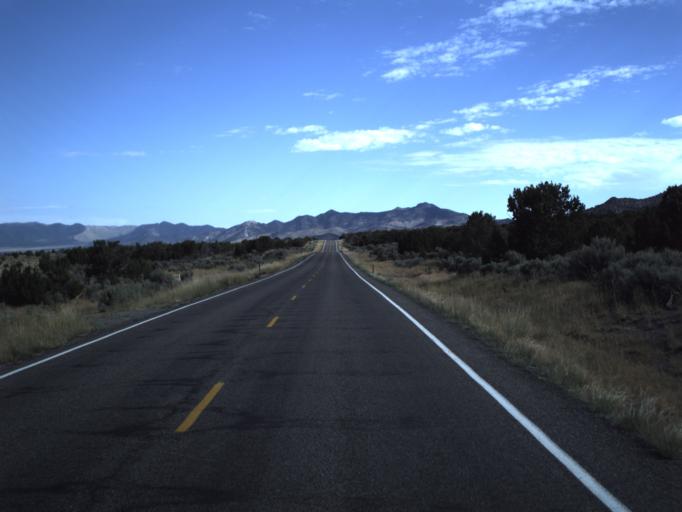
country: US
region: Utah
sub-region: Juab County
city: Mona
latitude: 39.8150
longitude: -112.1423
